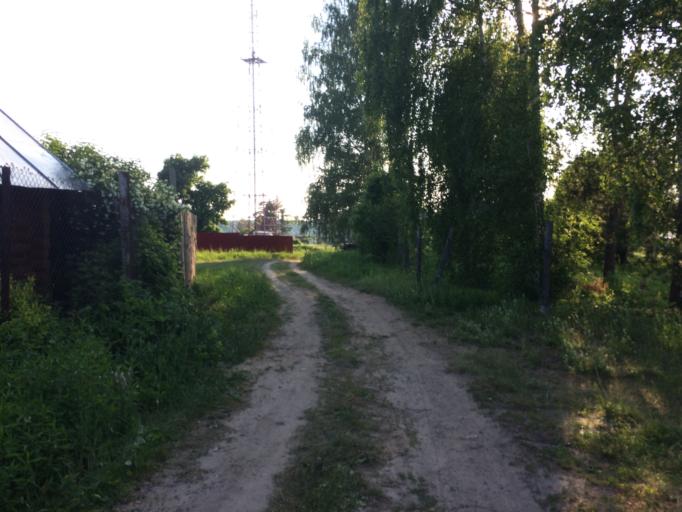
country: RU
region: Mariy-El
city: Mochalishche
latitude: 56.5426
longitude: 48.4089
